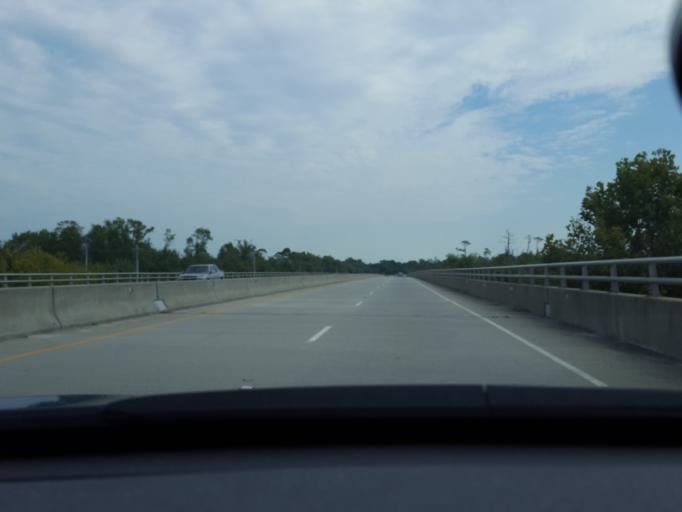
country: US
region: North Carolina
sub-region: Chowan County
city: Edenton
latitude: 36.0533
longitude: -76.6836
